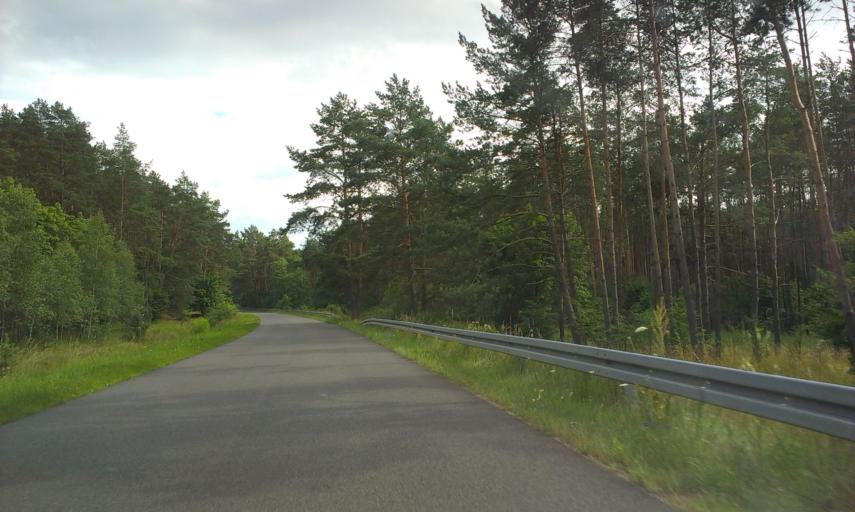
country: PL
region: Greater Poland Voivodeship
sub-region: Powiat zlotowski
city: Okonek
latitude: 53.4940
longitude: 16.9834
